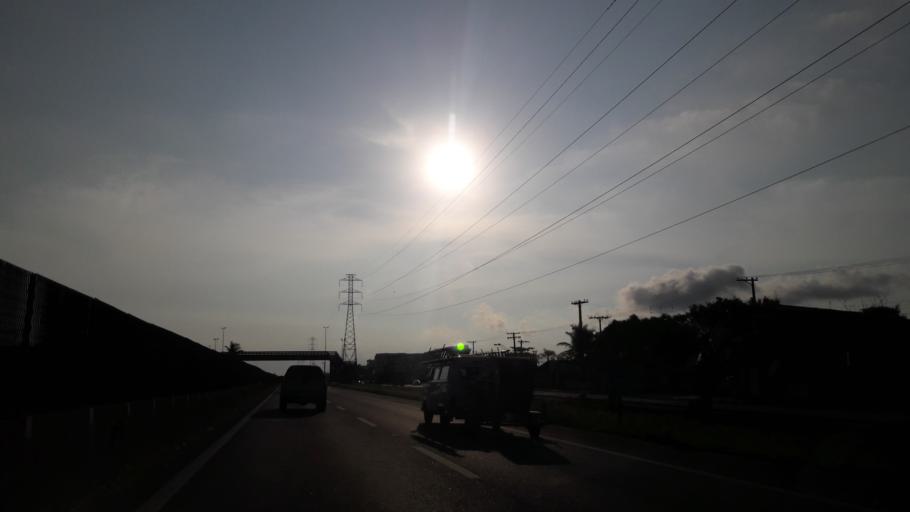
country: BR
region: Sao Paulo
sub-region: Mongagua
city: Mongagua
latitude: -24.1351
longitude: -46.7028
